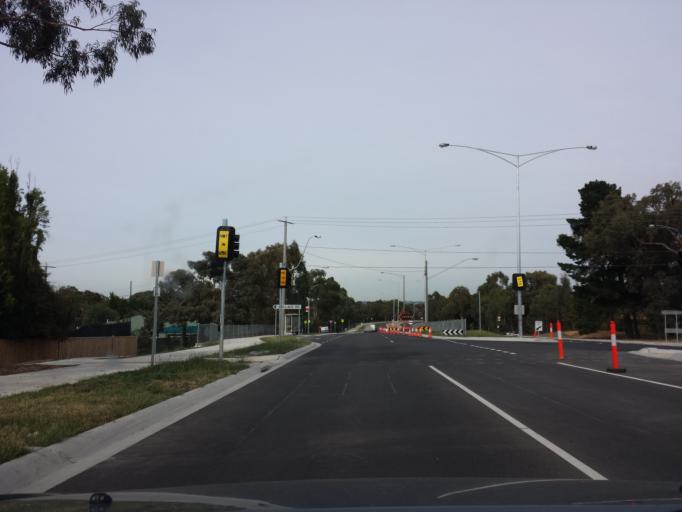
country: AU
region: Victoria
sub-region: Knox
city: Knoxfield
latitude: -37.8751
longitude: 145.2444
